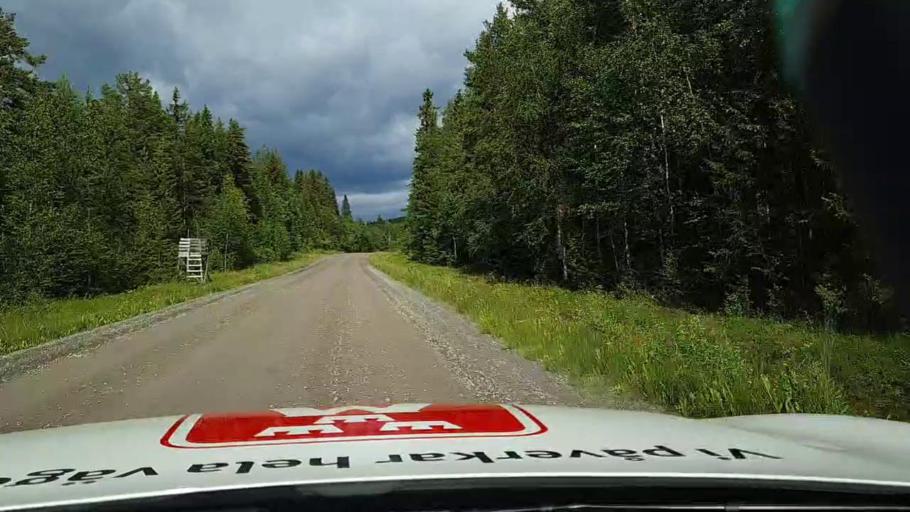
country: SE
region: Vaesternorrland
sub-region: Solleftea Kommun
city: As
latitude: 63.4718
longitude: 16.2831
